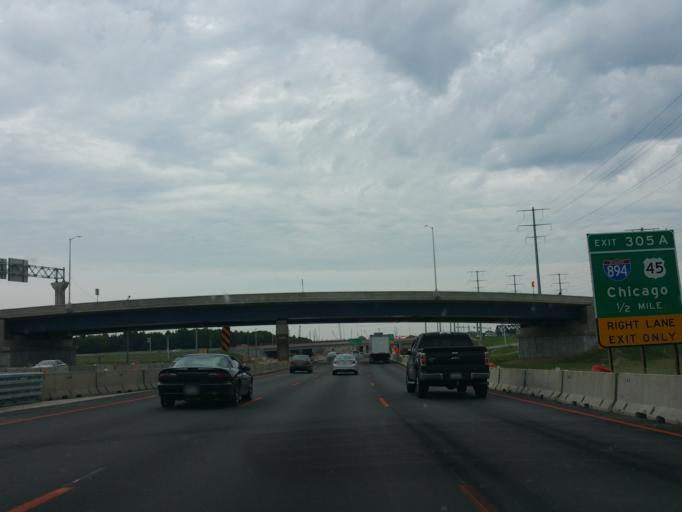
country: US
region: Wisconsin
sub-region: Waukesha County
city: Elm Grove
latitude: 43.0302
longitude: -88.0507
